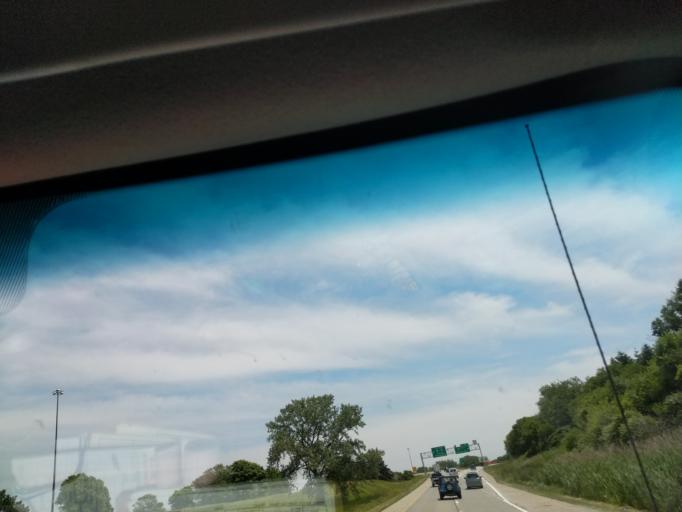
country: US
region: Iowa
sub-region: Polk County
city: Clive
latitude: 41.5915
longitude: -93.7826
